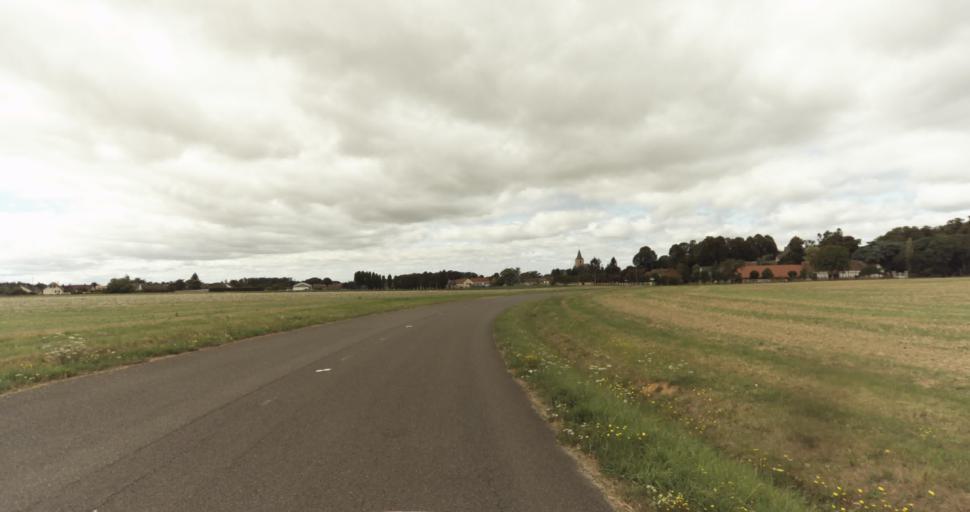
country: FR
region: Haute-Normandie
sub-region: Departement de l'Eure
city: Evreux
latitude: 48.9357
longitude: 1.2053
